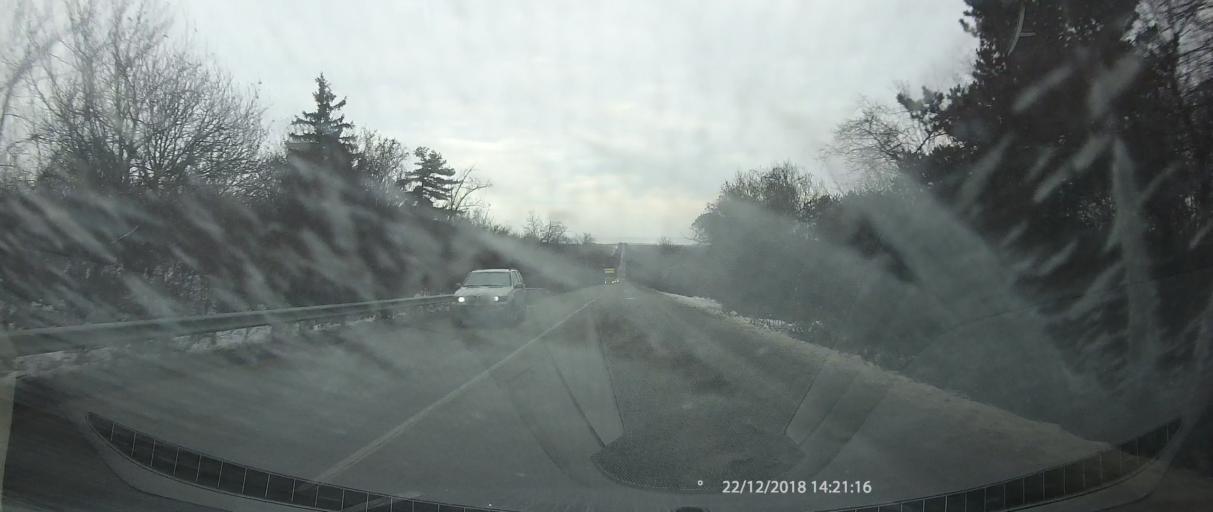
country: BG
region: Pleven
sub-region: Obshtina Pordim
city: Pordim
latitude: 43.4187
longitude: 24.7818
